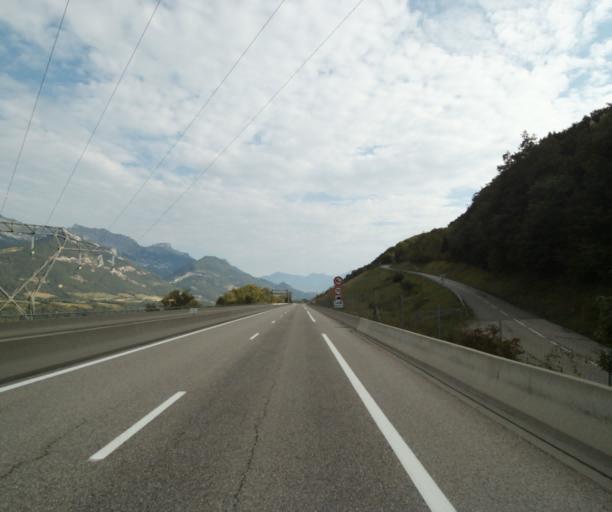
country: FR
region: Rhone-Alpes
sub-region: Departement de l'Isere
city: Le Gua
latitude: 44.9802
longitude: 5.6466
